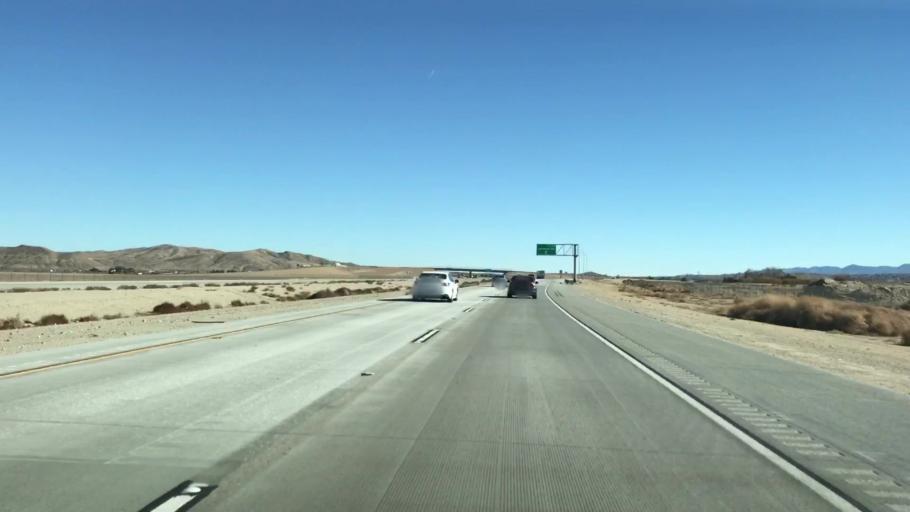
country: US
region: California
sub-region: San Bernardino County
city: Lenwood
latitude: 34.9153
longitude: -117.1286
